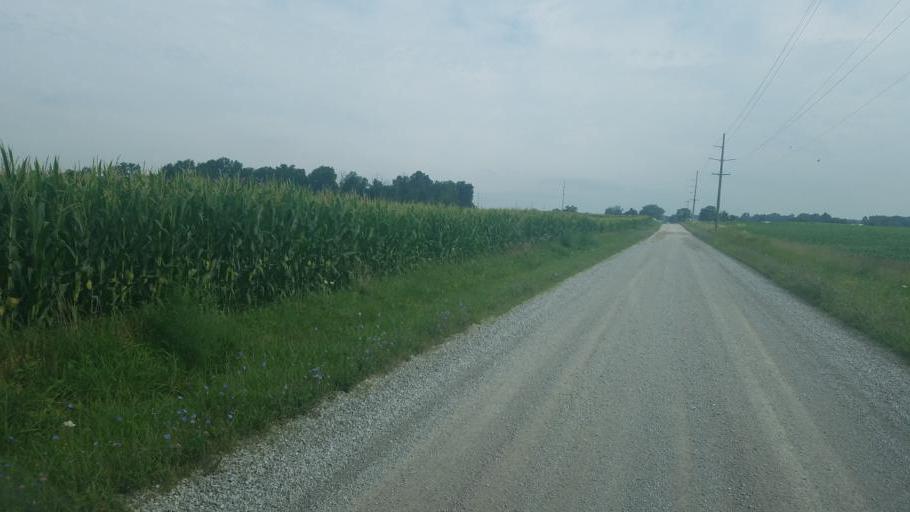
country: US
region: Ohio
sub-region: Delaware County
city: Ashley
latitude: 40.3838
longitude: -82.9124
